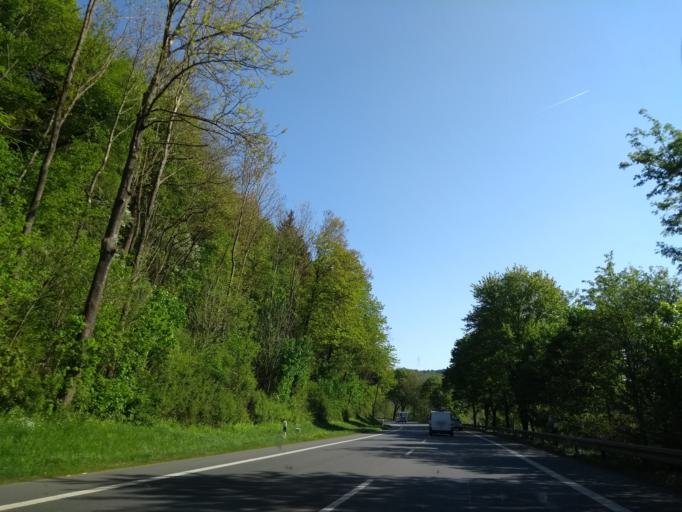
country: DE
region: Hesse
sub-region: Regierungsbezirk Kassel
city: Frankenau
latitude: 51.1259
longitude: 8.8734
